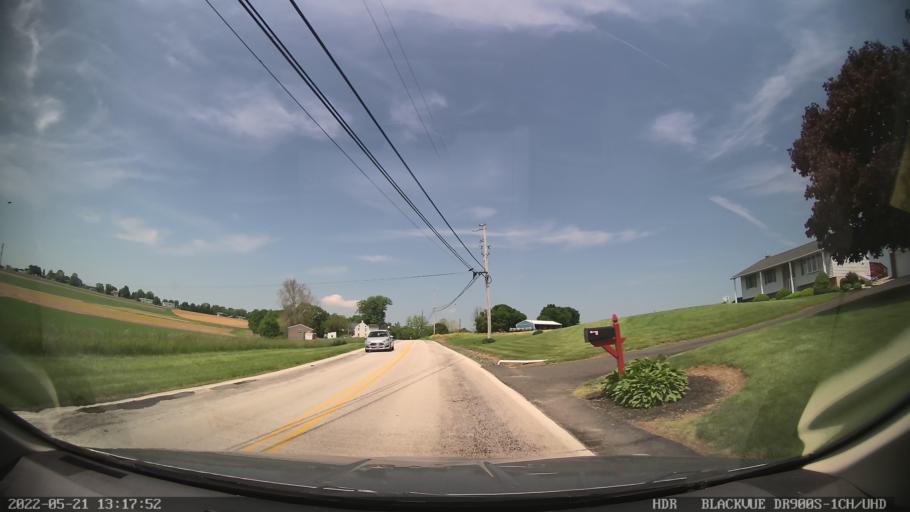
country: US
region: Pennsylvania
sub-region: Berks County
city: Bally
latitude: 40.3631
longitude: -75.5919
